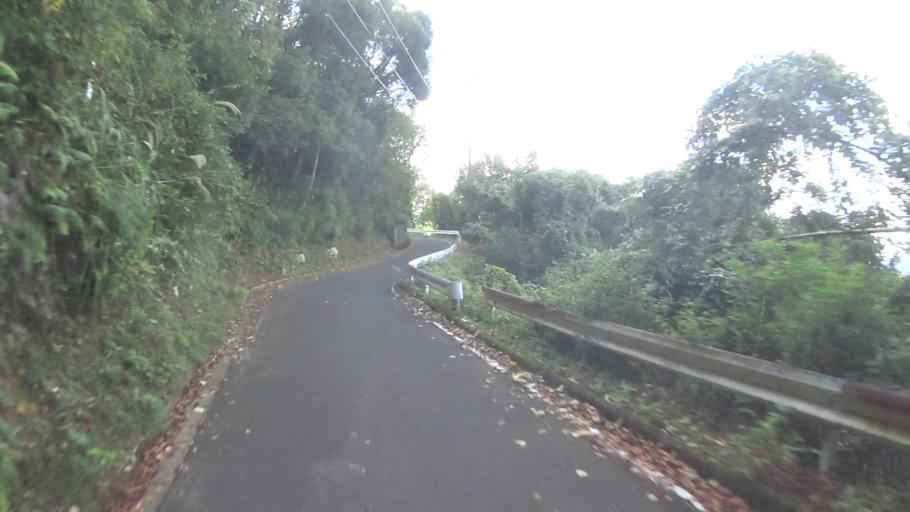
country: JP
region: Kyoto
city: Maizuru
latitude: 35.5683
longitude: 135.4141
